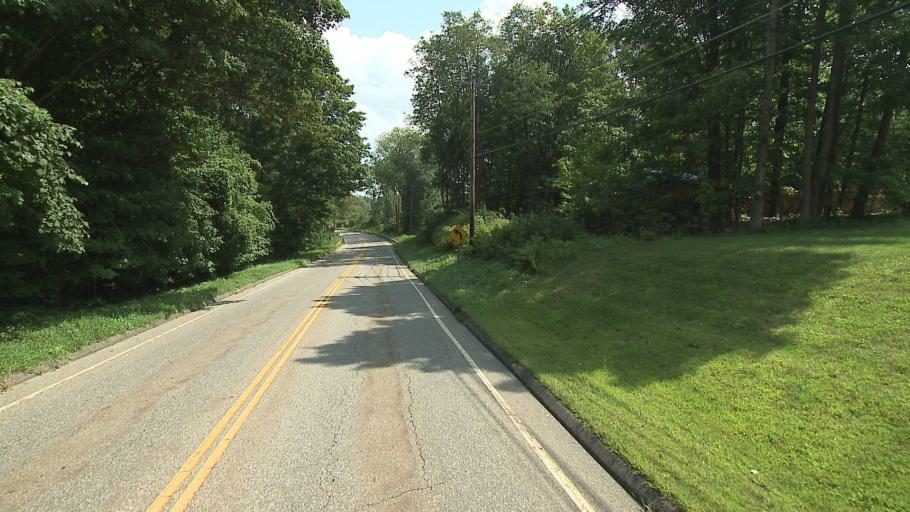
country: US
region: Connecticut
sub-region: Litchfield County
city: Bethlehem Village
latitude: 41.6879
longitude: -73.1788
